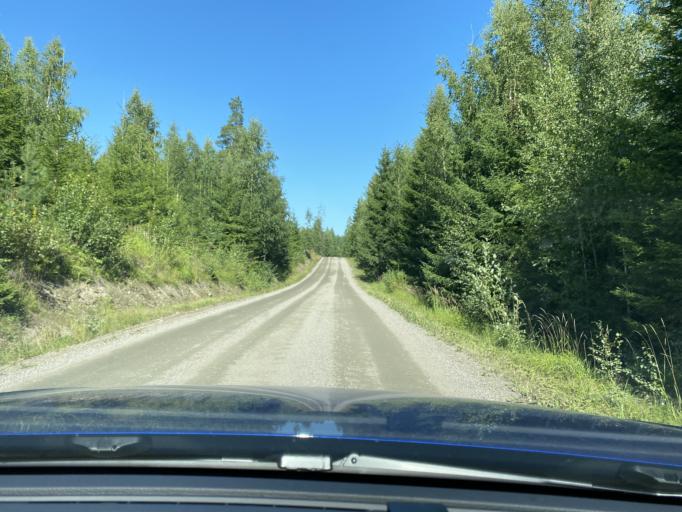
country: FI
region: Central Finland
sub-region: Jyvaeskylae
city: Korpilahti
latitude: 61.8674
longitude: 25.4233
